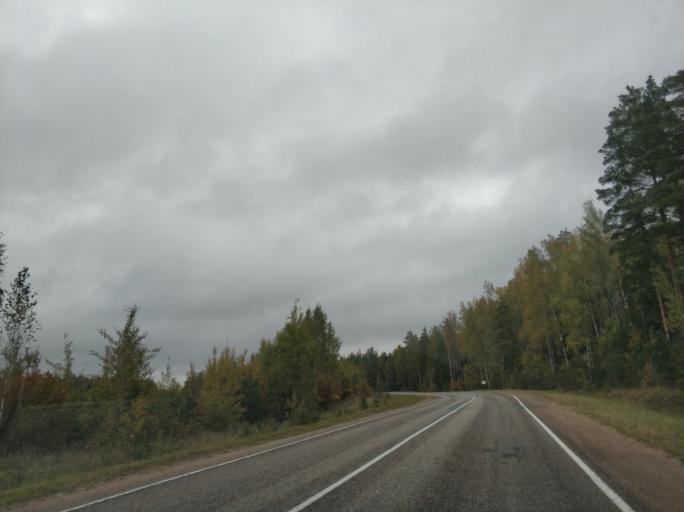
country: RU
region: Pskov
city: Opochka
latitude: 56.5087
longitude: 28.6644
